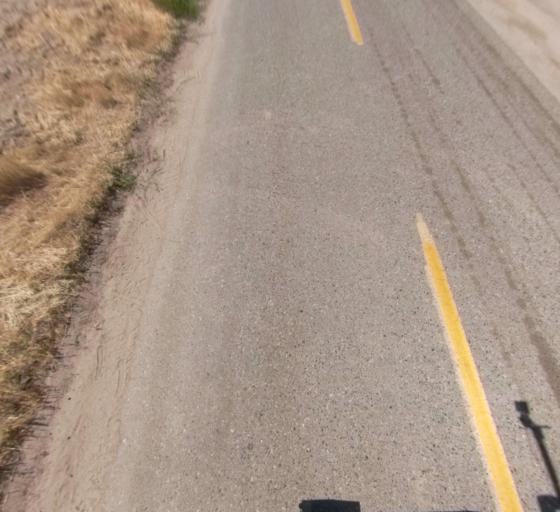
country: US
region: California
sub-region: Fresno County
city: Biola
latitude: 36.8581
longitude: -120.0283
